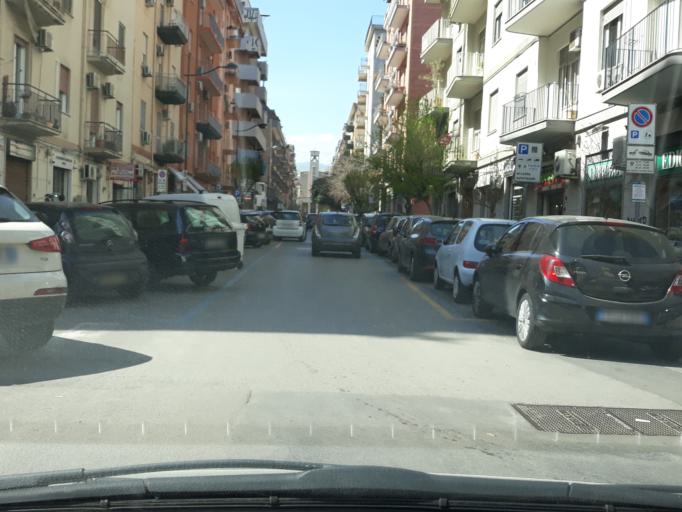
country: IT
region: Sicily
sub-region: Palermo
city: Palermo
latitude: 38.1363
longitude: 13.3462
